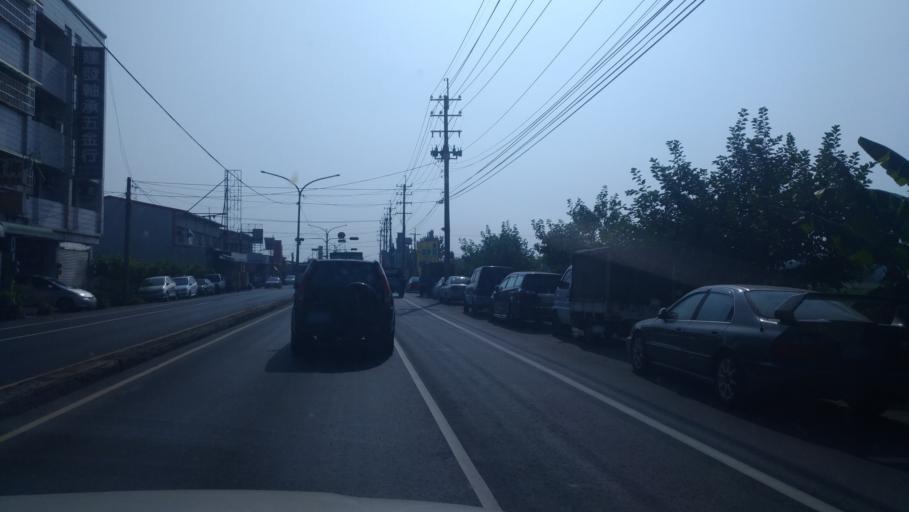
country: TW
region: Taiwan
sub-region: Chiayi
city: Jiayi Shi
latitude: 23.5150
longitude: 120.4302
